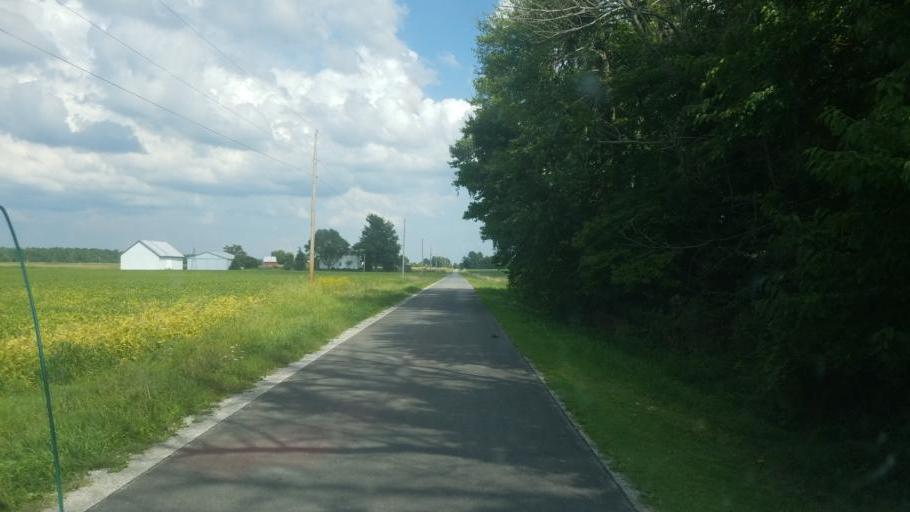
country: US
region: Ohio
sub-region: Huron County
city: Willard
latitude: 41.0082
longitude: -82.8908
